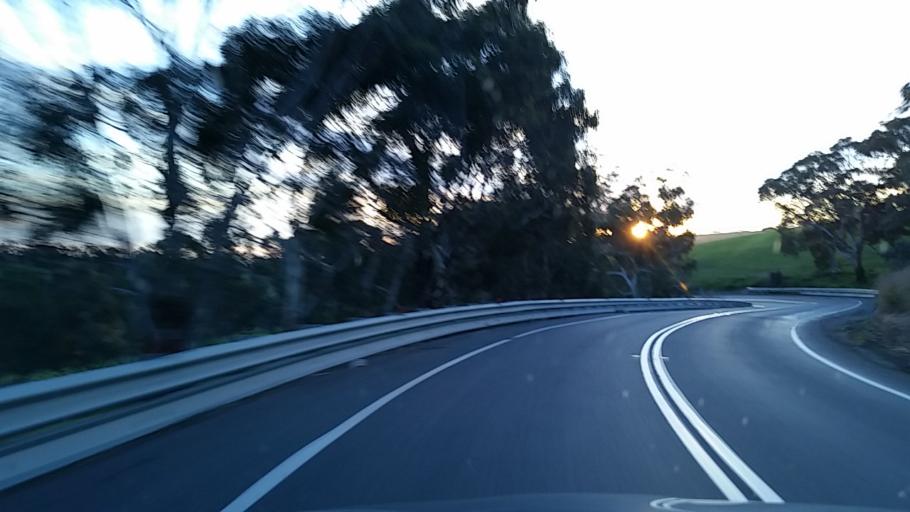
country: AU
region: South Australia
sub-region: Yankalilla
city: Normanville
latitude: -35.4223
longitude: 138.4148
